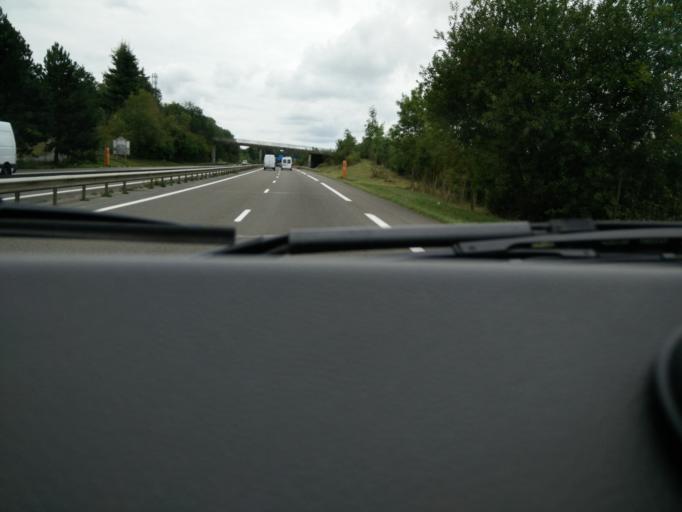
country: FR
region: Champagne-Ardenne
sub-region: Departement des Ardennes
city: Sedan
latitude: 49.6912
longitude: 4.9195
